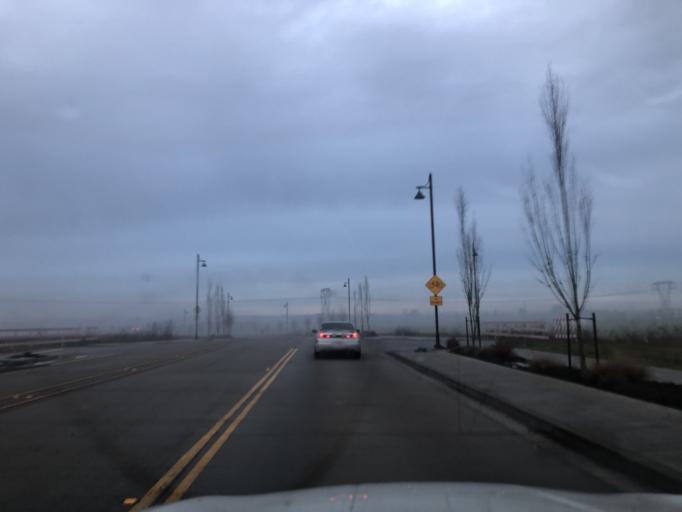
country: US
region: Oregon
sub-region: Washington County
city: Aloha
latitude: 45.4924
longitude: -122.8949
